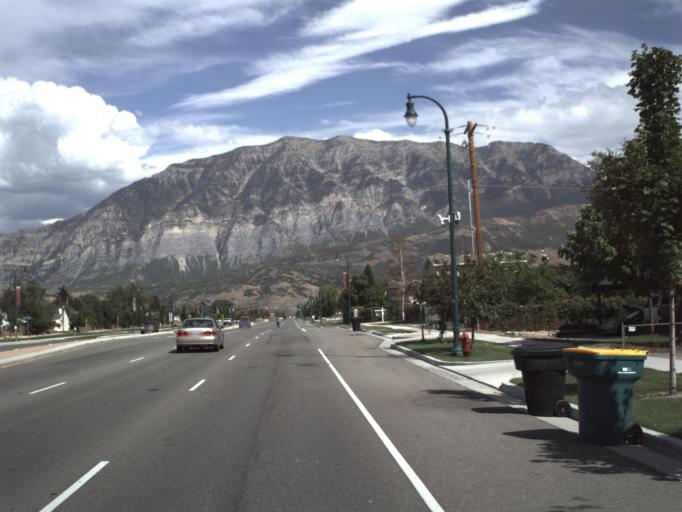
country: US
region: Utah
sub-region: Utah County
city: Orem
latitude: 40.3119
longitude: -111.6953
